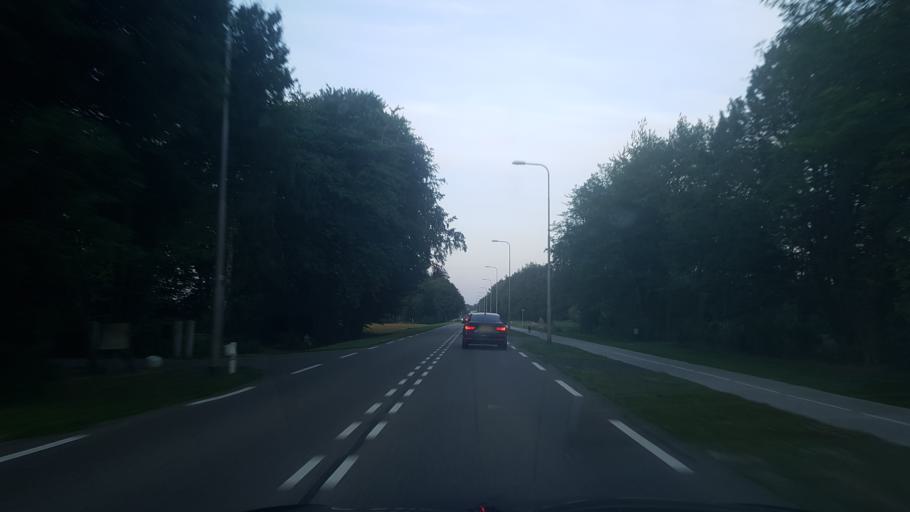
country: NL
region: Flevoland
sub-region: Gemeente Noordoostpolder
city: Emmeloord
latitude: 52.7239
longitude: 5.7302
